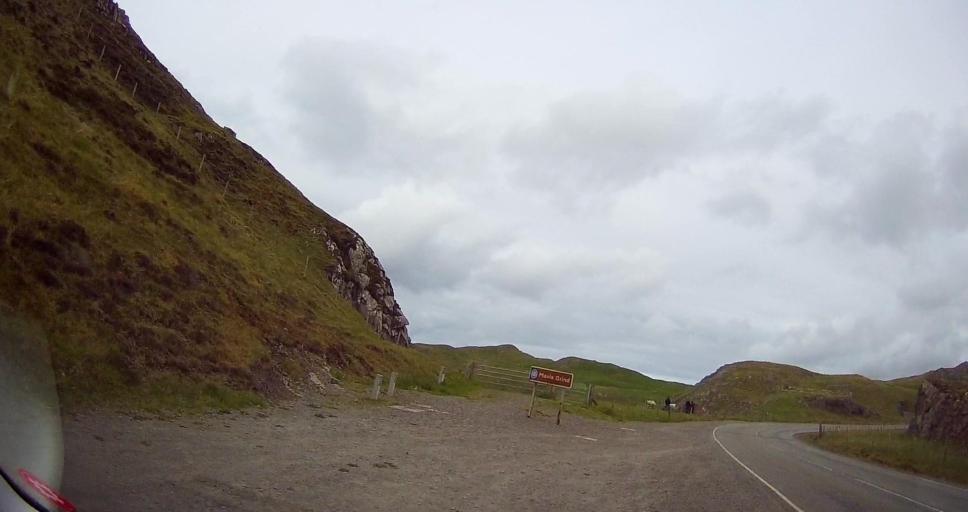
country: GB
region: Scotland
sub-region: Shetland Islands
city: Lerwick
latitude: 60.3974
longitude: -1.3838
